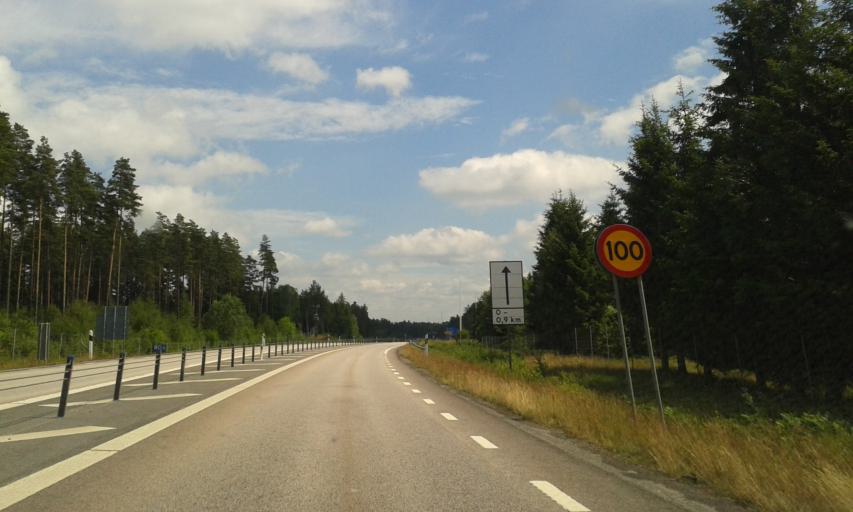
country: SE
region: Kronoberg
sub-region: Alvesta Kommun
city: Alvesta
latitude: 56.9141
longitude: 14.4882
